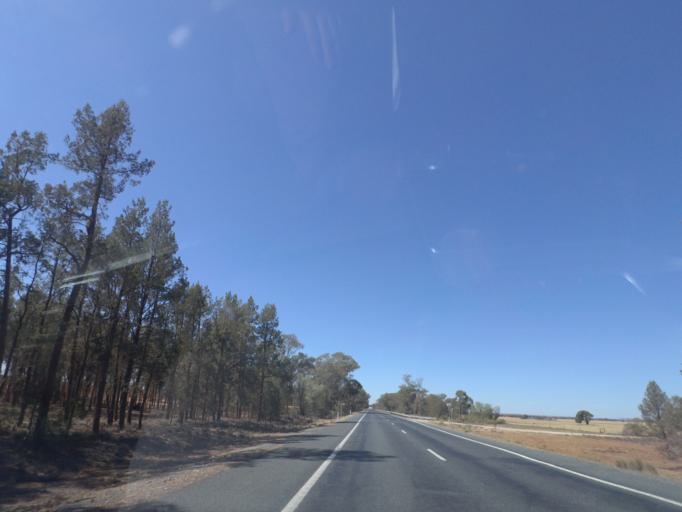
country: AU
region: New South Wales
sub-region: Bland
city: West Wyalong
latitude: -34.2144
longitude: 147.1080
